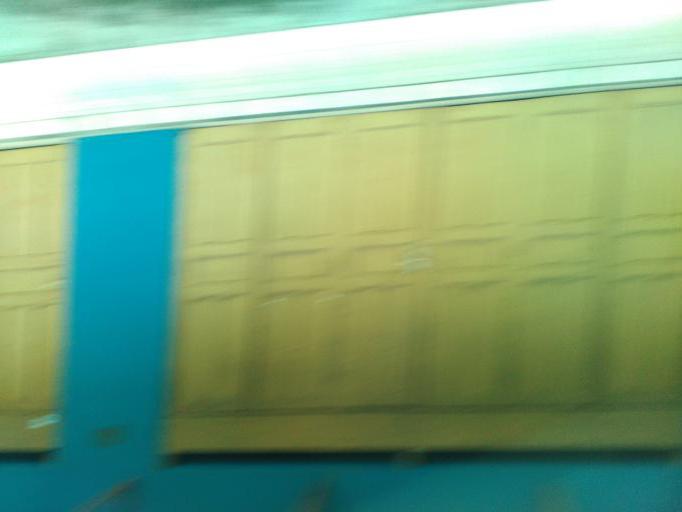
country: ID
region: Central Java
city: Delanggu
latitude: -7.6175
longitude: 110.7008
